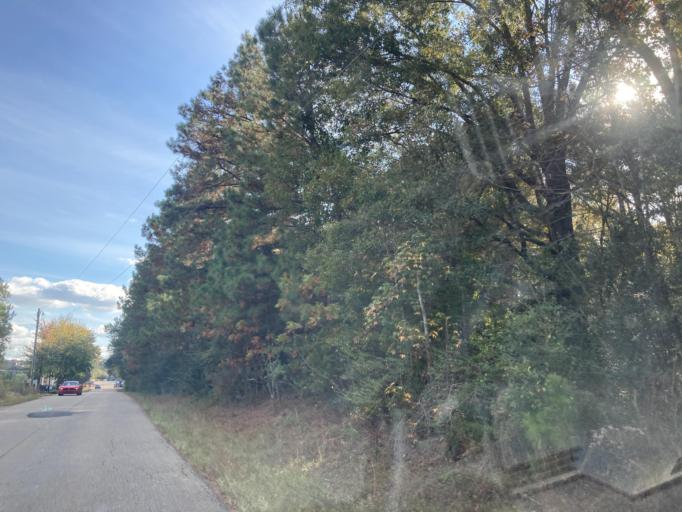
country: US
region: Mississippi
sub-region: Lamar County
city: West Hattiesburg
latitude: 31.3196
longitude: -89.3548
